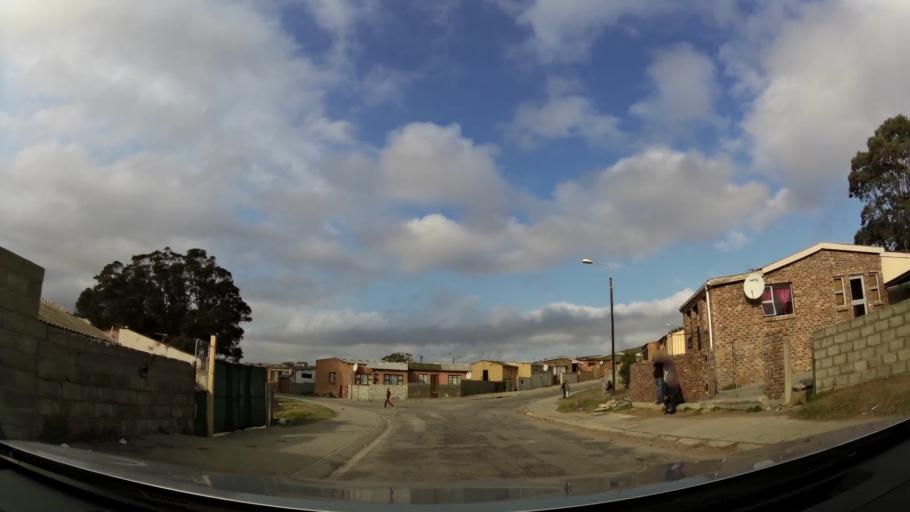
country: ZA
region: Eastern Cape
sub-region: Nelson Mandela Bay Metropolitan Municipality
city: Port Elizabeth
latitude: -33.9147
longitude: 25.5455
